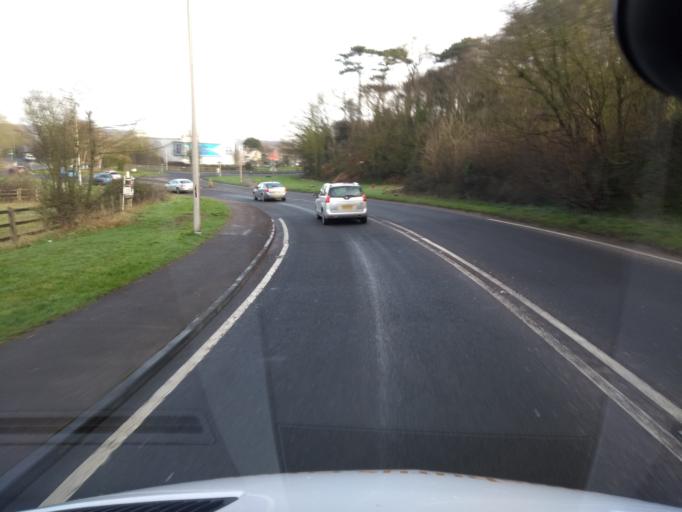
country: GB
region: England
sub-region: North Somerset
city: Bleadon
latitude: 51.3203
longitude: -2.9691
